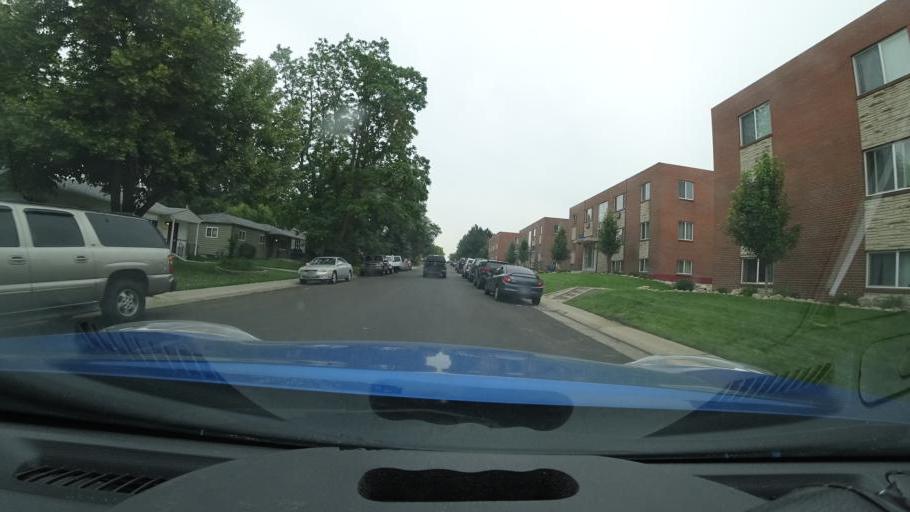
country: US
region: Colorado
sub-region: Arapahoe County
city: Glendale
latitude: 39.6804
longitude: -104.9285
